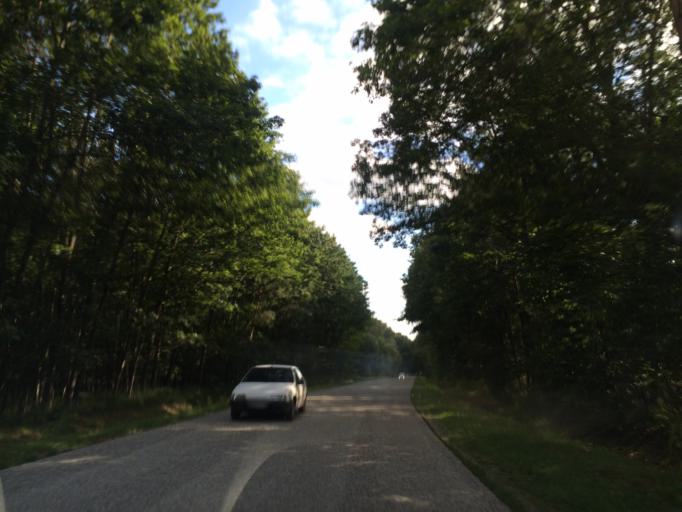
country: FR
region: Alsace
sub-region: Departement du Bas-Rhin
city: Soufflenheim
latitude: 48.8590
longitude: 7.9351
